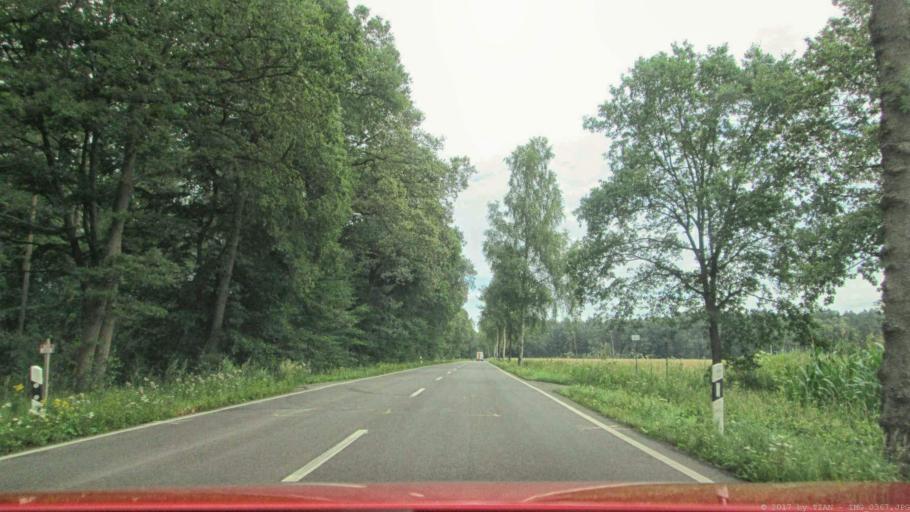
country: DE
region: Lower Saxony
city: Ruhen
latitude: 52.5054
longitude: 10.8829
